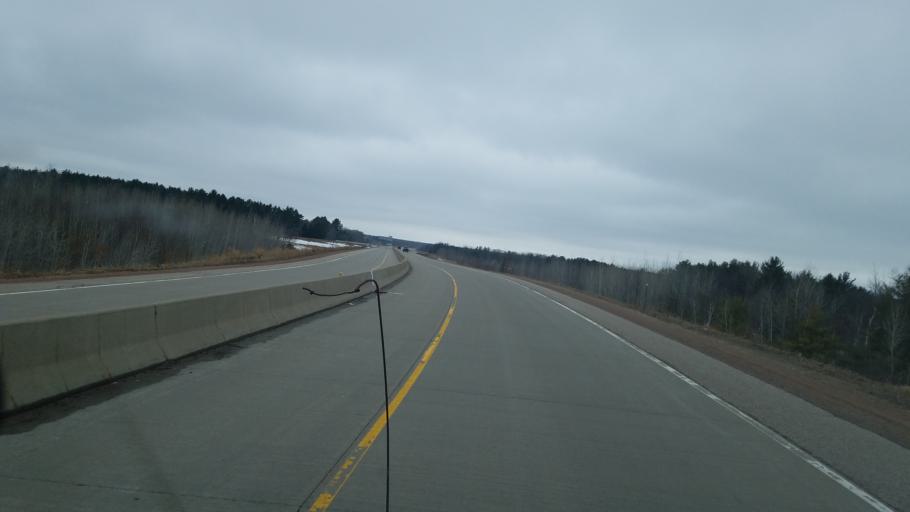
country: US
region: Wisconsin
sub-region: Portage County
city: Stevens Point
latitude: 44.5980
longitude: -89.6111
